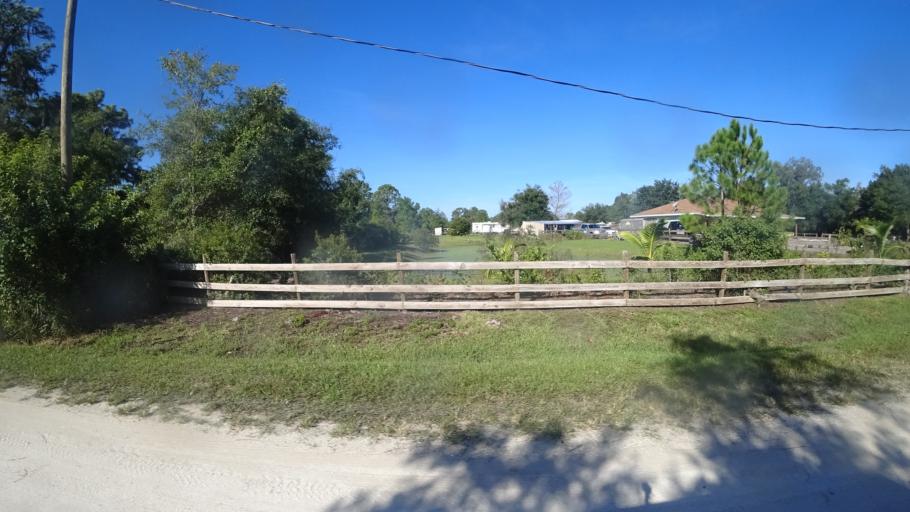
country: US
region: Florida
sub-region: Hillsborough County
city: Sun City Center
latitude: 27.6447
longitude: -82.3532
